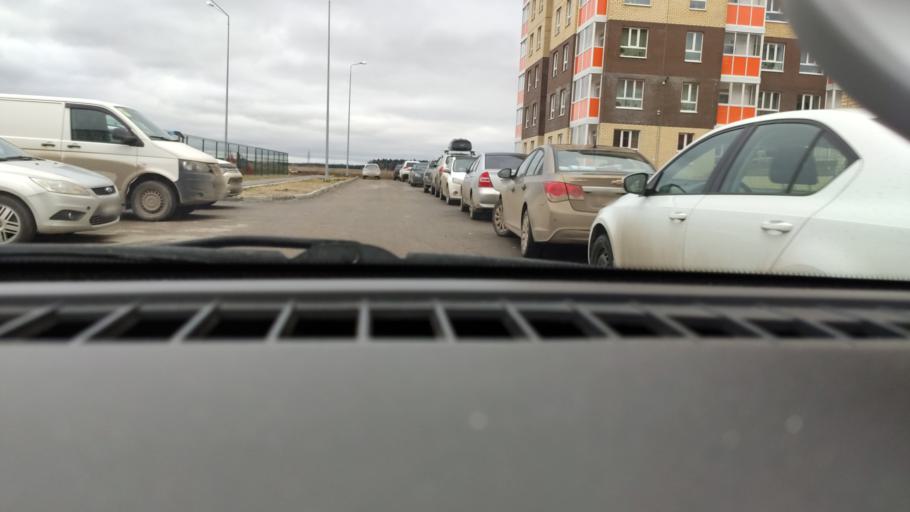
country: RU
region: Perm
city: Perm
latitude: 58.0032
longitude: 56.3378
